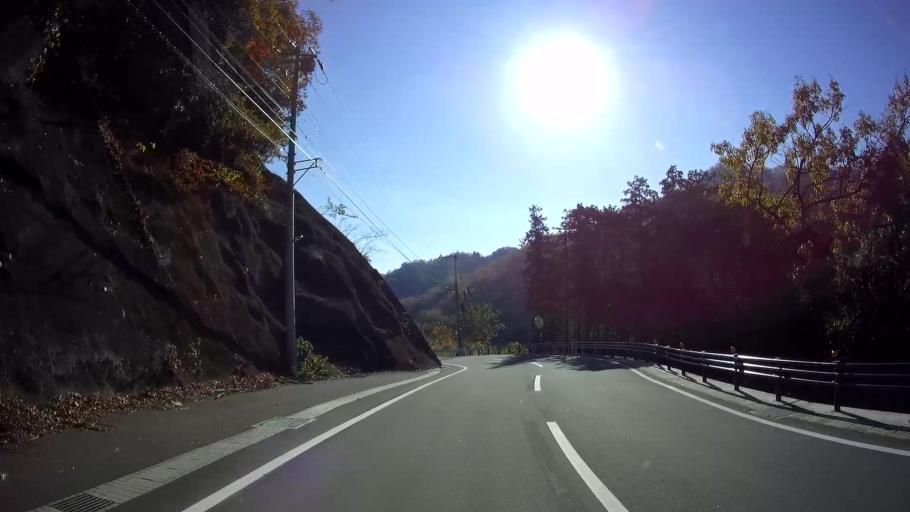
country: JP
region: Yamanashi
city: Uenohara
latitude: 35.5944
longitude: 139.1204
